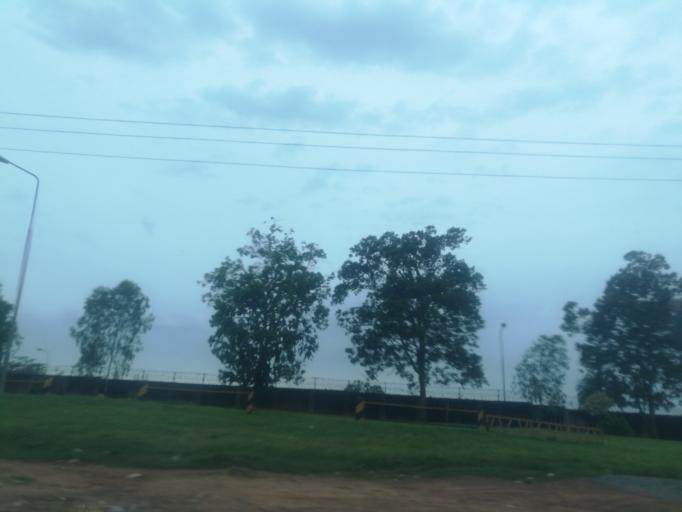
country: NG
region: Oyo
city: Ibadan
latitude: 7.3941
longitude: 3.9664
